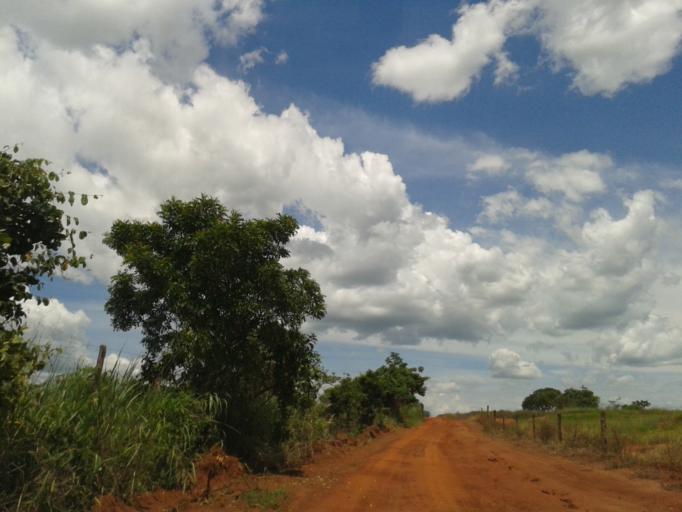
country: BR
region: Minas Gerais
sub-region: Ituiutaba
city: Ituiutaba
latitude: -18.8710
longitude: -49.4873
